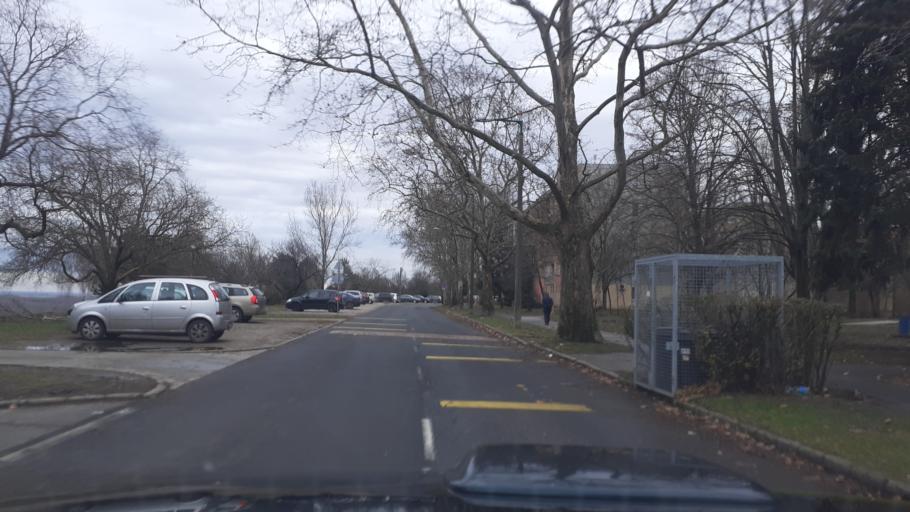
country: HU
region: Fejer
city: Dunaujvaros
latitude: 46.9721
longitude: 18.9388
